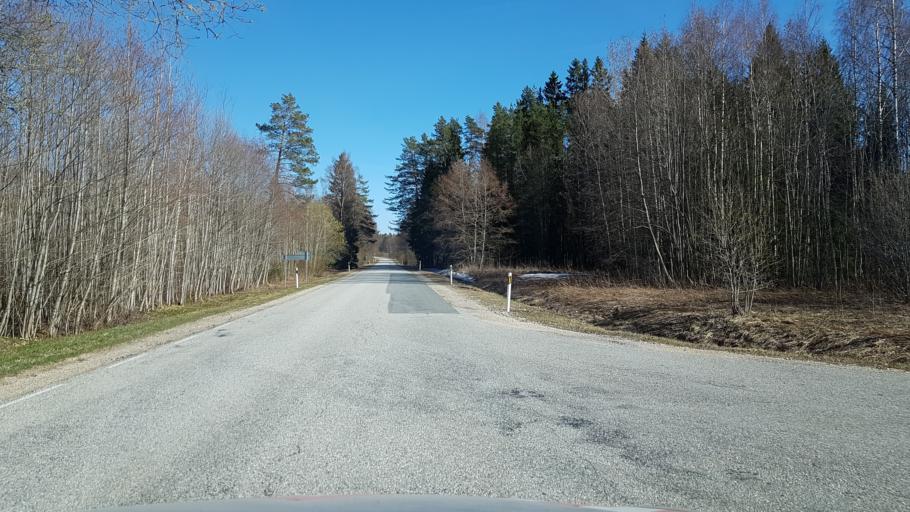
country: EE
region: Ida-Virumaa
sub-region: Aseri vald
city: Aseri
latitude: 59.2323
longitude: 26.7017
